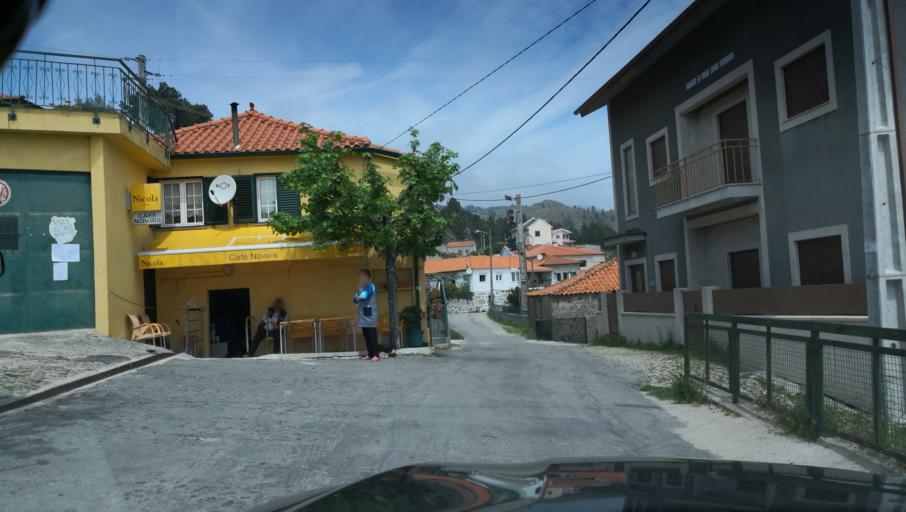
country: PT
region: Vila Real
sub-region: Vila Real
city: Vila Real
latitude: 41.3137
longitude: -7.7970
